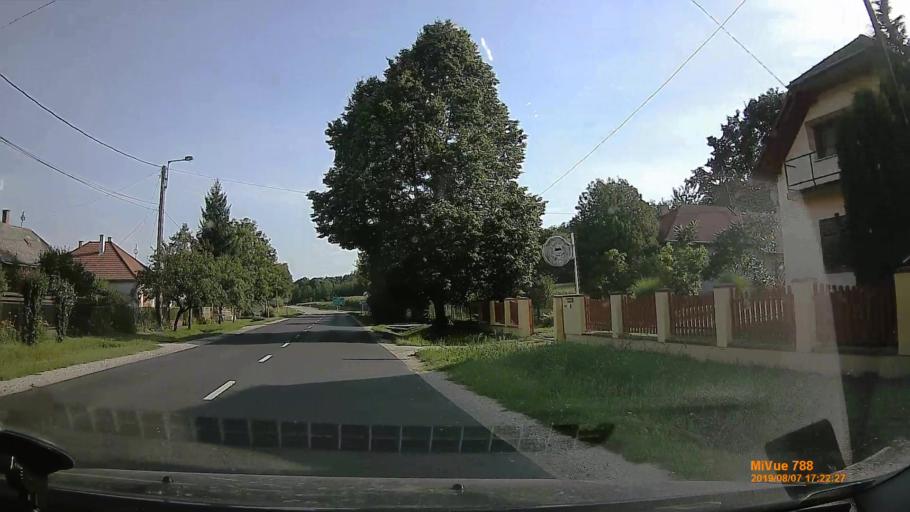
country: HU
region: Zala
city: Nagykanizsa
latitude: 46.5777
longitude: 16.9182
